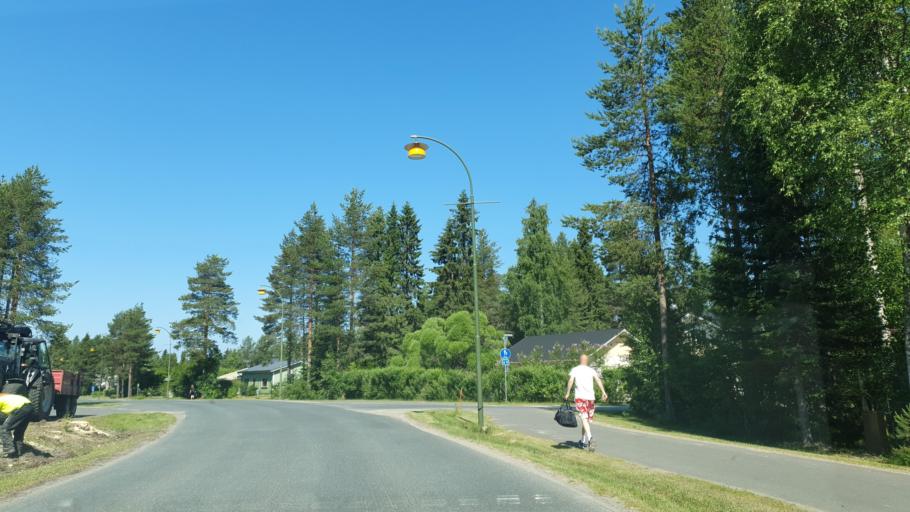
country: FI
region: Lapland
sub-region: Rovaniemi
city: Ranua
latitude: 65.9308
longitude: 26.5155
